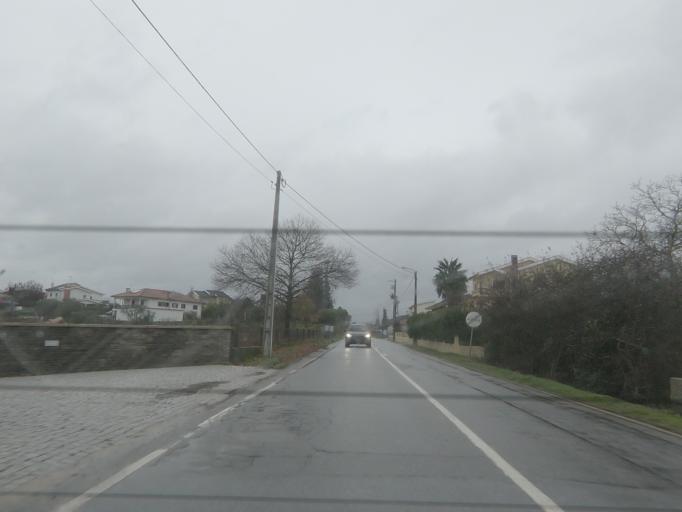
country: PT
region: Vila Real
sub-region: Vila Real
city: Vila Real
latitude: 41.2697
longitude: -7.7048
